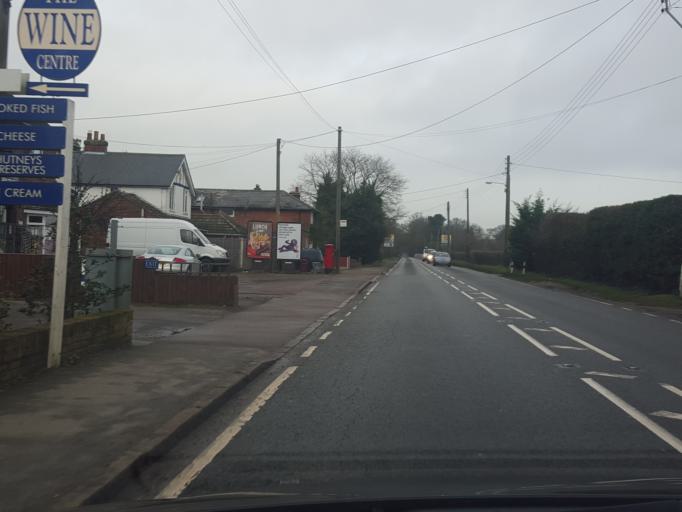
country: GB
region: England
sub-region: Essex
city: Great Horkesley
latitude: 51.9394
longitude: 0.8758
